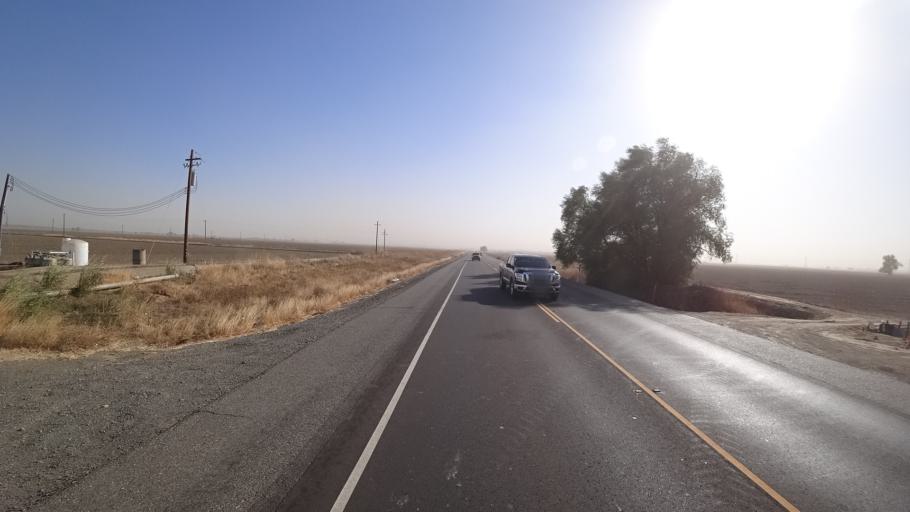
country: US
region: California
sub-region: Yolo County
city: Woodland
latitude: 38.7705
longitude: -121.7287
